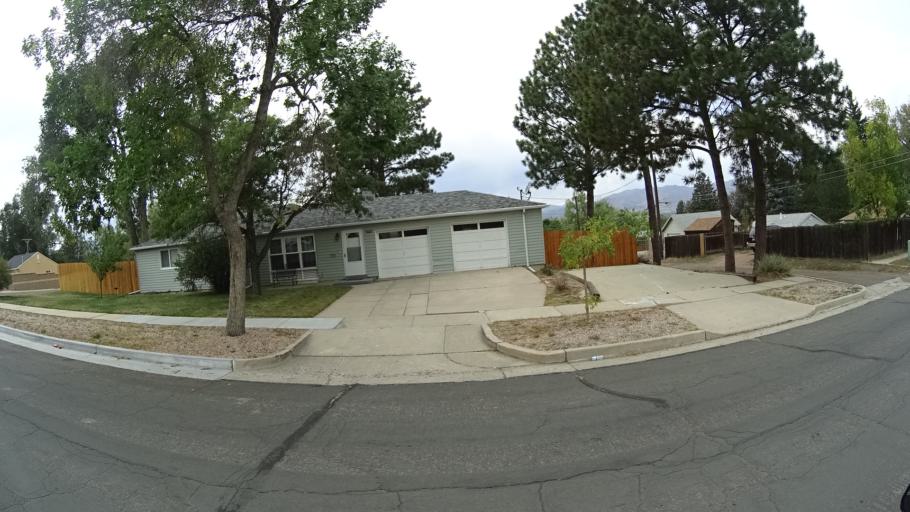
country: US
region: Colorado
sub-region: El Paso County
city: Colorado Springs
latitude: 38.8647
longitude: -104.7897
